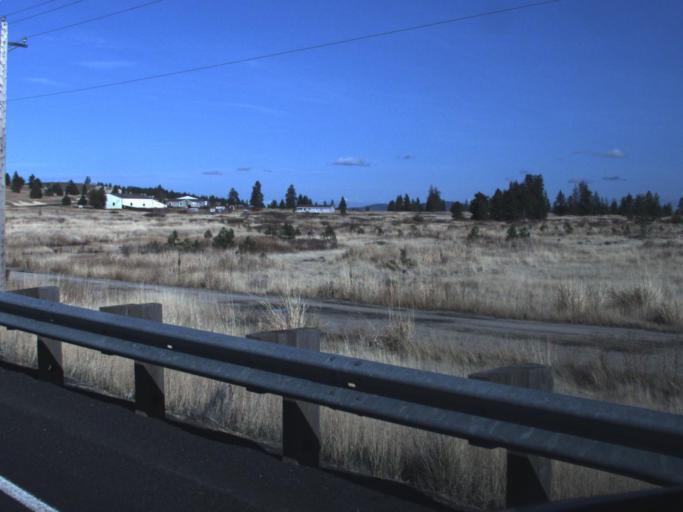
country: US
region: Washington
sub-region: Lincoln County
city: Davenport
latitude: 47.7785
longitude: -118.1736
